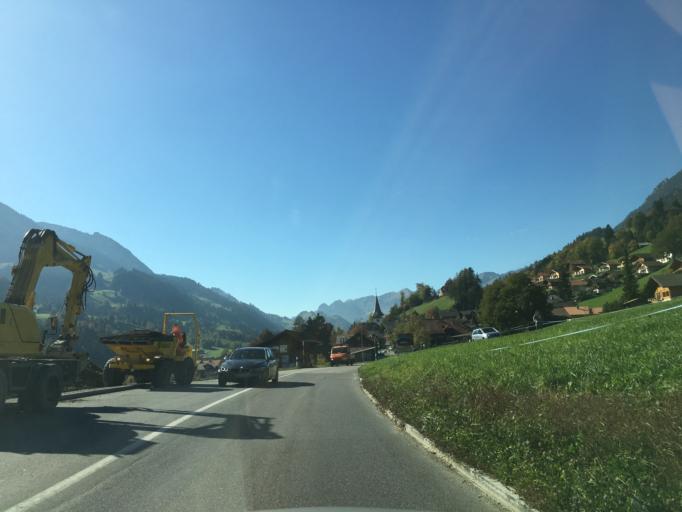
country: CH
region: Bern
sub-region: Frutigen-Niedersimmental District
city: Erlenbach im Simmental
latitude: 46.6614
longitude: 7.5593
